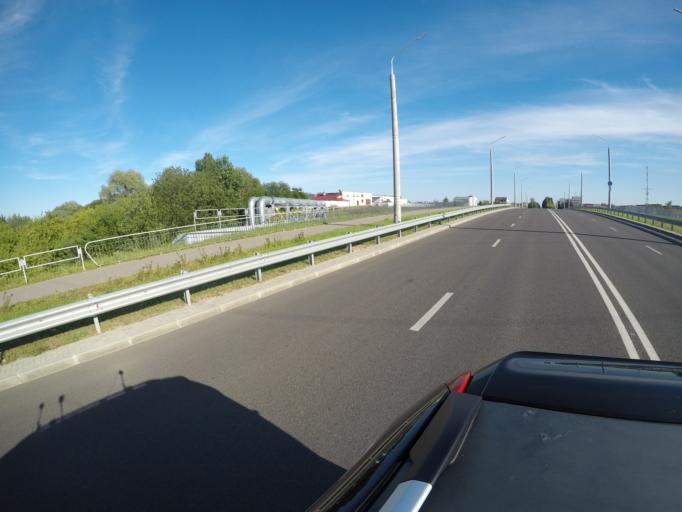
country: BY
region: Grodnenskaya
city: Hrodna
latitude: 53.7175
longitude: 23.8243
